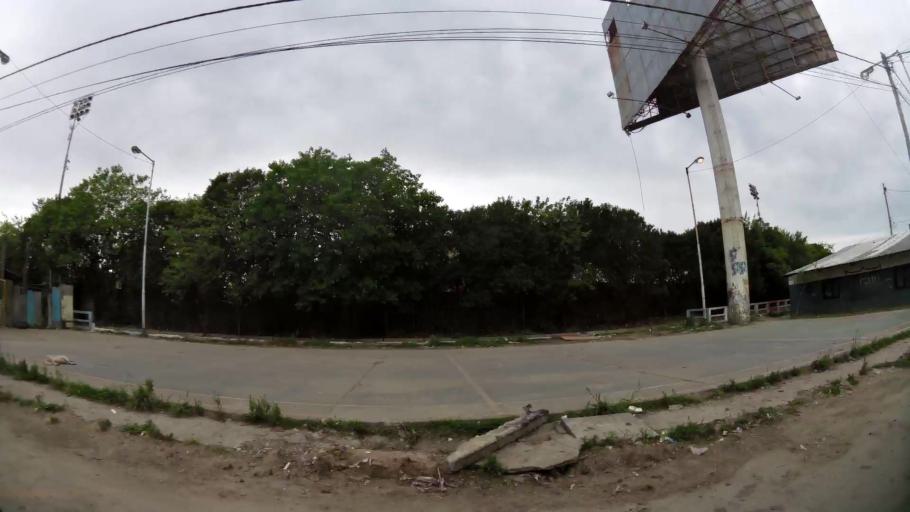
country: AR
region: Buenos Aires
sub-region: Partido de Avellaneda
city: Avellaneda
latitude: -34.6509
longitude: -58.3543
